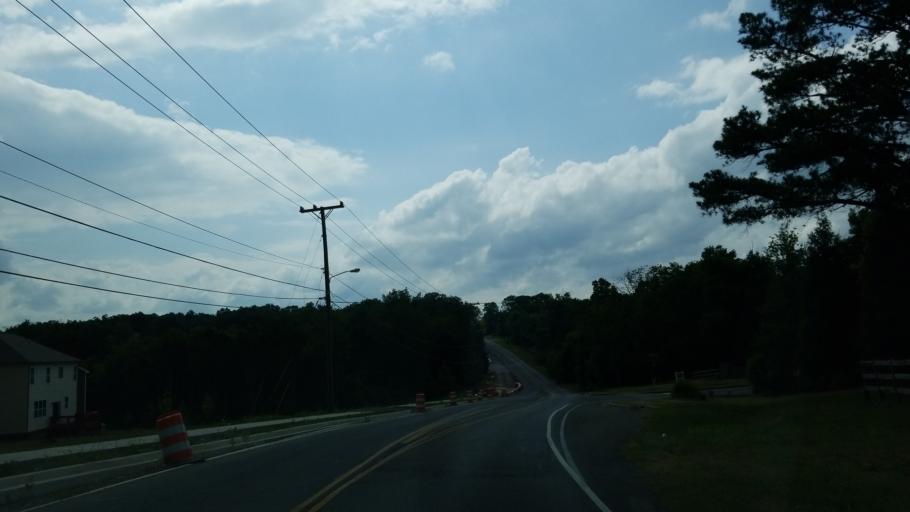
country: US
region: Tennessee
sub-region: Rutherford County
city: La Vergne
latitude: 36.0635
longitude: -86.6133
